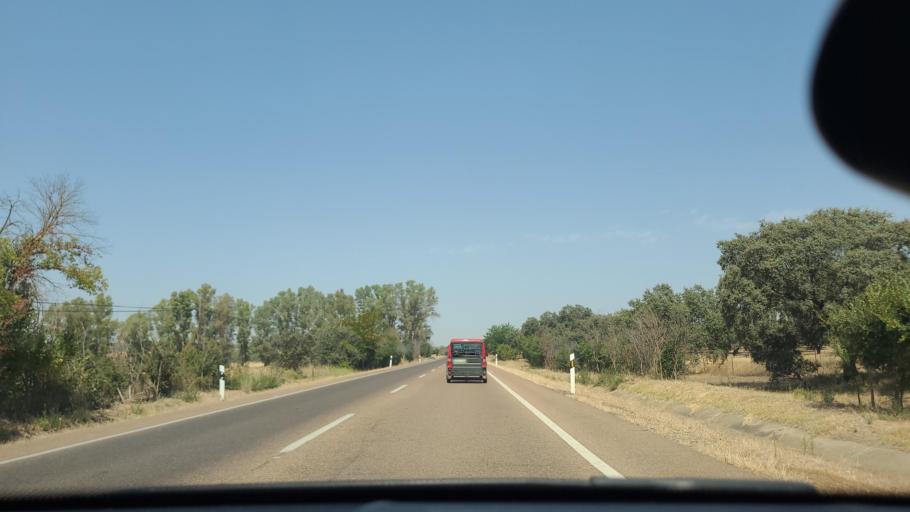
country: ES
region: Extremadura
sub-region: Provincia de Badajoz
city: Badajoz
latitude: 38.8351
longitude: -6.9228
